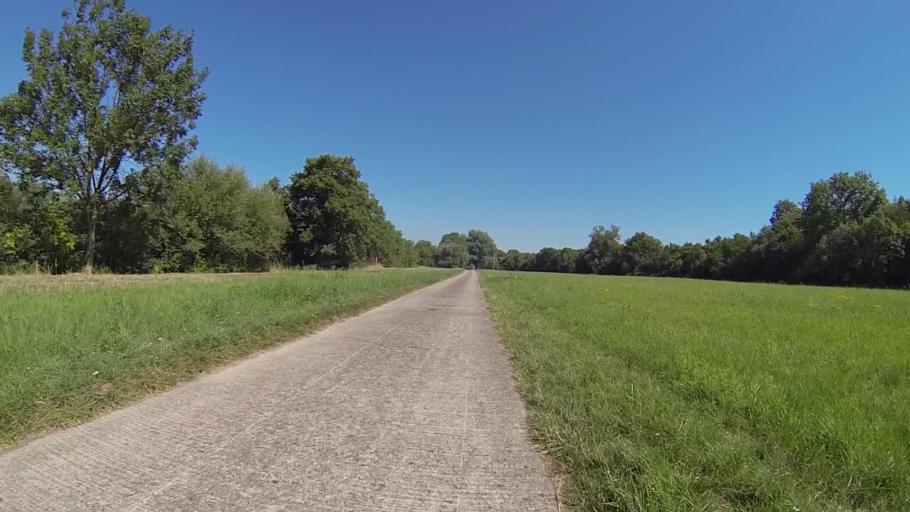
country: LU
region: Grevenmacher
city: Schengen
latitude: 49.4840
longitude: 6.3692
